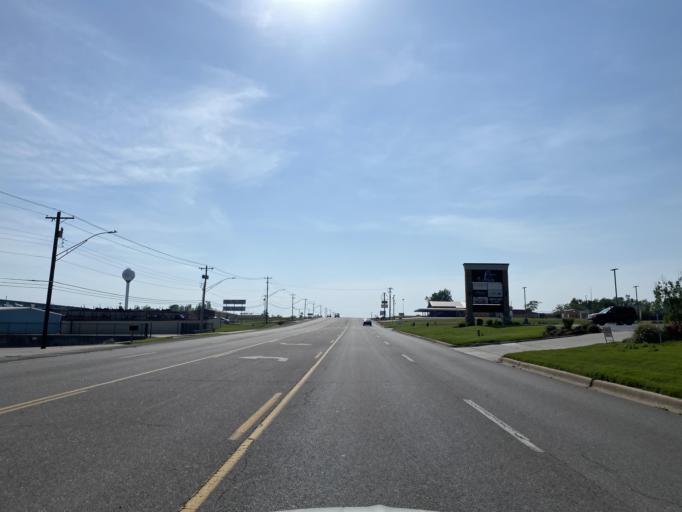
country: US
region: Oklahoma
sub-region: Oklahoma County
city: Nicoma Park
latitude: 35.4931
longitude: -97.3378
